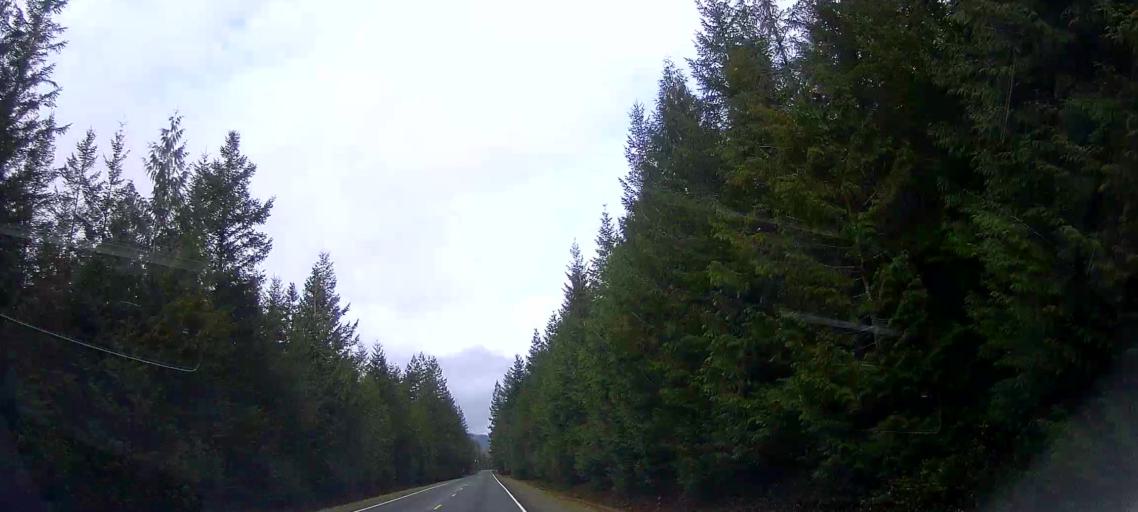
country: US
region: Washington
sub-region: Snohomish County
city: Darrington
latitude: 48.5105
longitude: -121.4557
